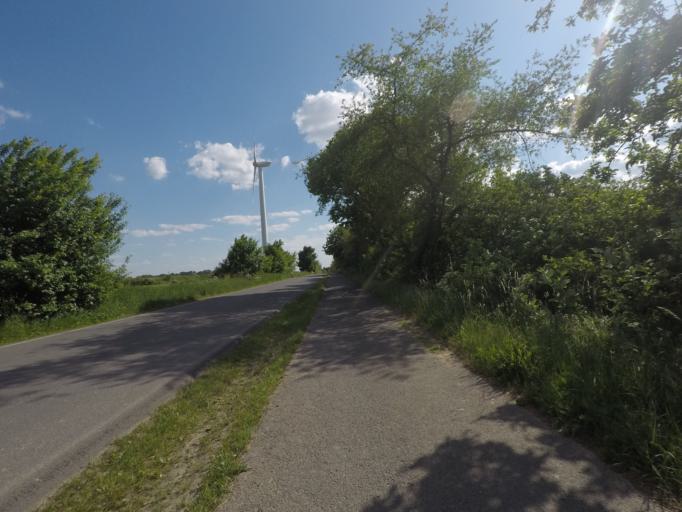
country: DE
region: Brandenburg
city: Britz
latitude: 52.8767
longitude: 13.7646
